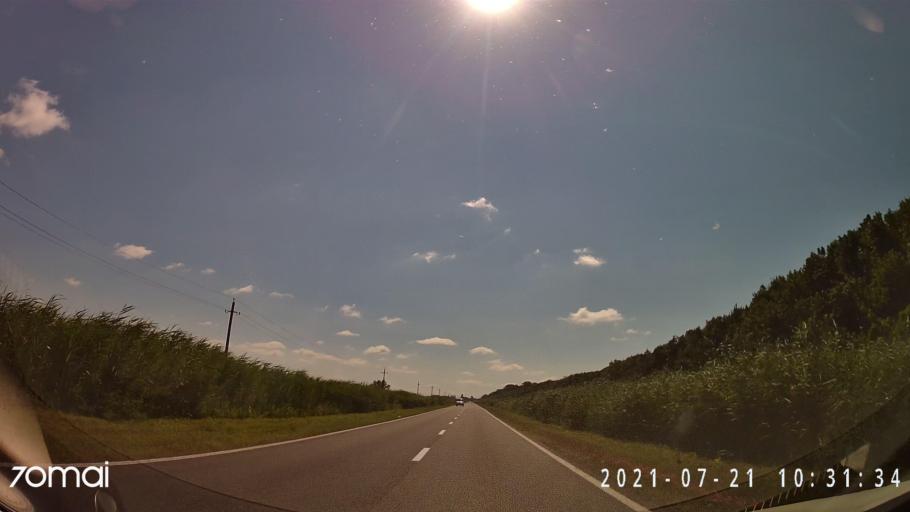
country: RO
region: Tulcea
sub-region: Oras Isaccea
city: Isaccea
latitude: 45.3072
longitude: 28.4044
